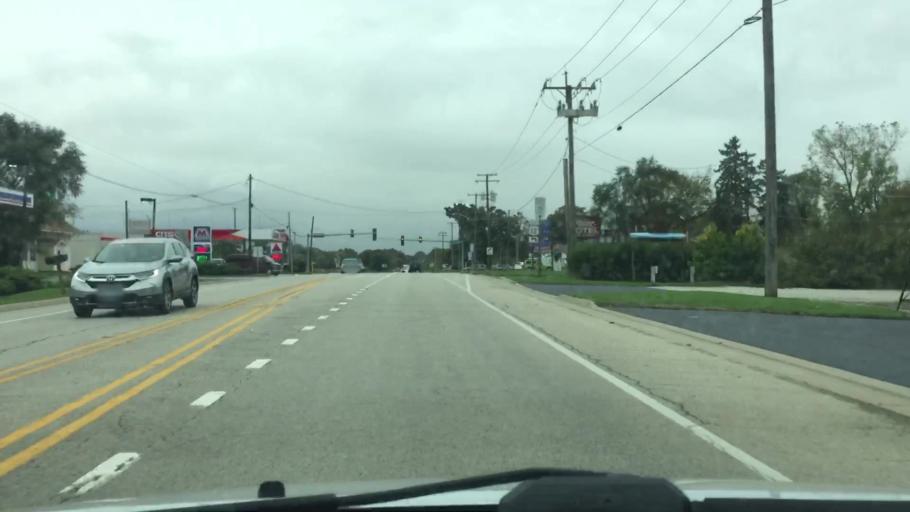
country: US
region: Illinois
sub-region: McHenry County
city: Richmond
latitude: 42.4524
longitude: -88.3059
